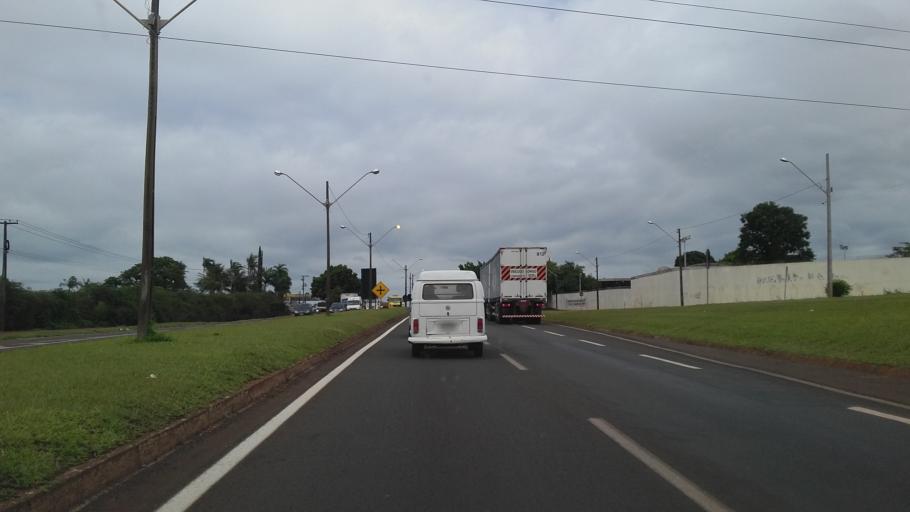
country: BR
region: Parana
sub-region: Londrina
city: Londrina
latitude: -23.2931
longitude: -51.1240
